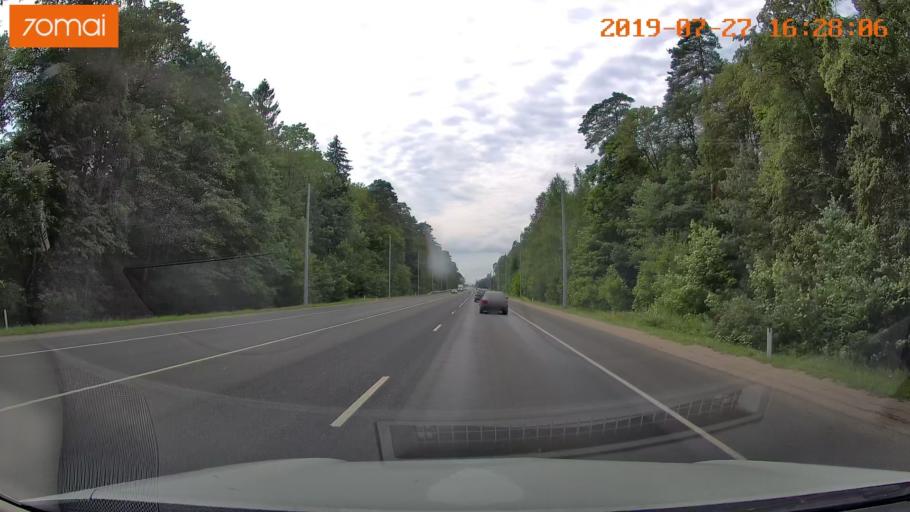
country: RU
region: Kaliningrad
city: Zheleznodorozhnyy
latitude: 54.6469
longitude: 21.3673
